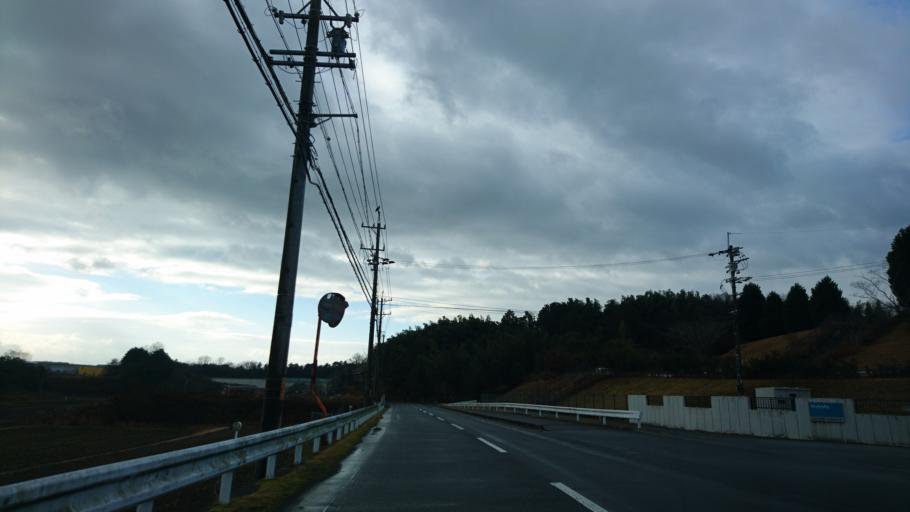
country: JP
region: Mie
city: Ueno-ebisumachi
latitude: 34.7190
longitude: 136.0771
